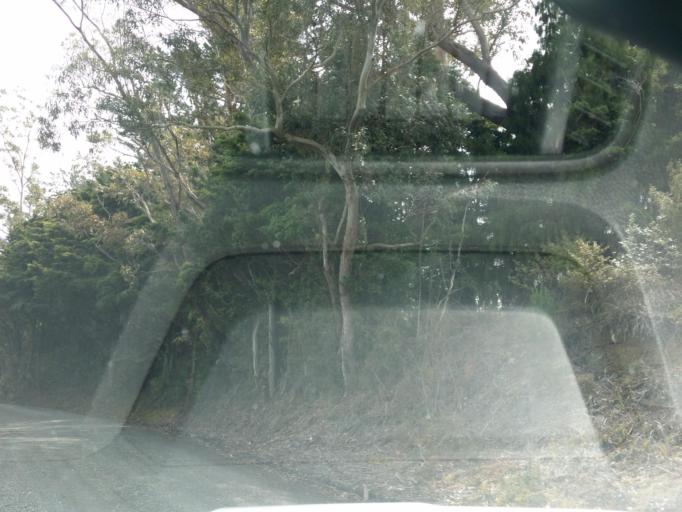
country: NZ
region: Northland
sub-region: Whangarei
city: Maungatapere
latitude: -35.9069
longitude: 174.1312
